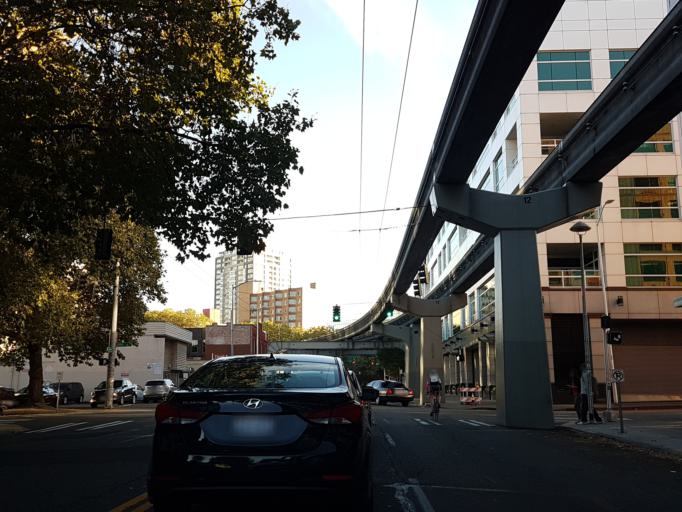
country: US
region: Washington
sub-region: King County
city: Seattle
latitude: 47.6200
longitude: -122.3476
